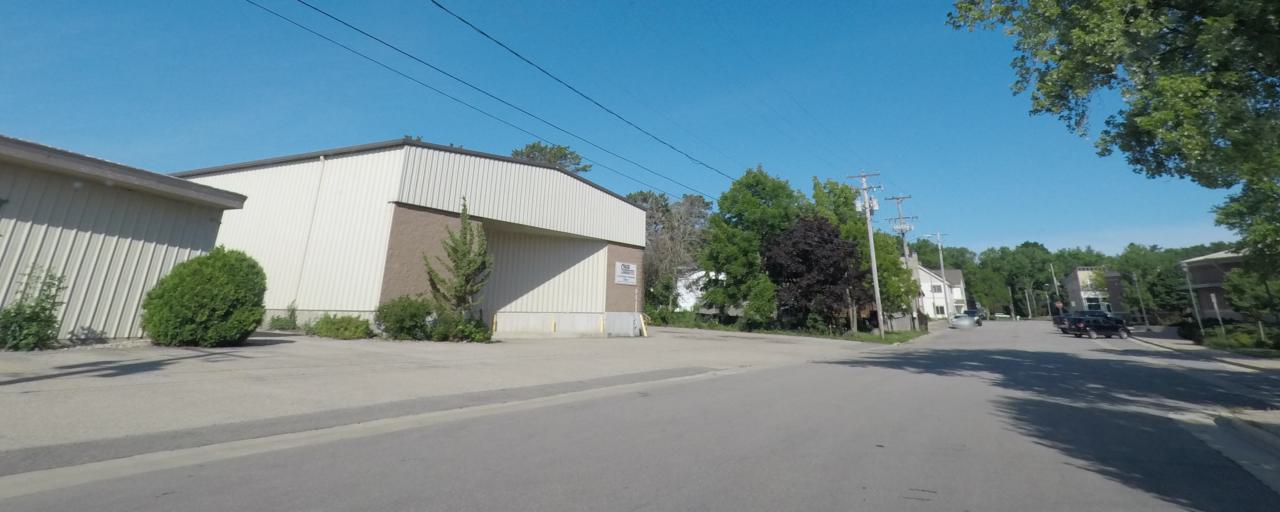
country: US
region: Wisconsin
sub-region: Dane County
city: McFarland
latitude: 43.0136
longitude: -89.2883
